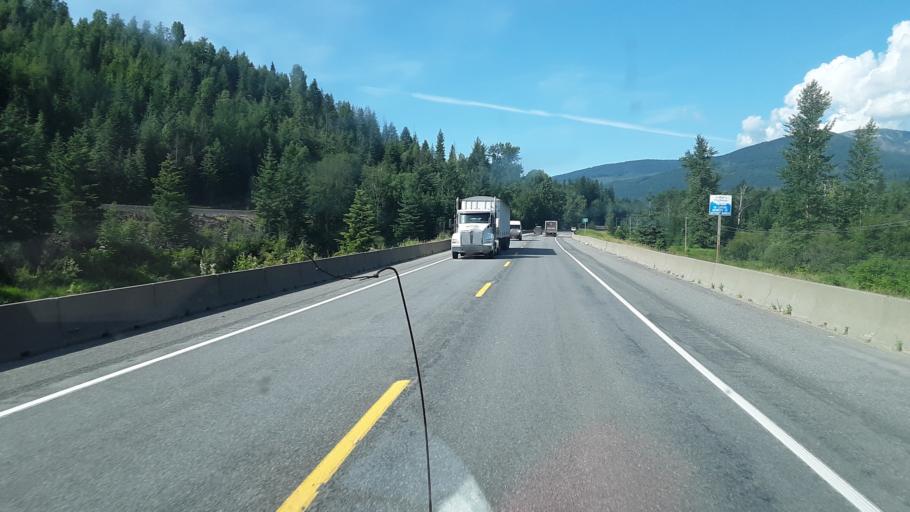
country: US
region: Idaho
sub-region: Bonner County
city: Ponderay
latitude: 48.4211
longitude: -116.5004
